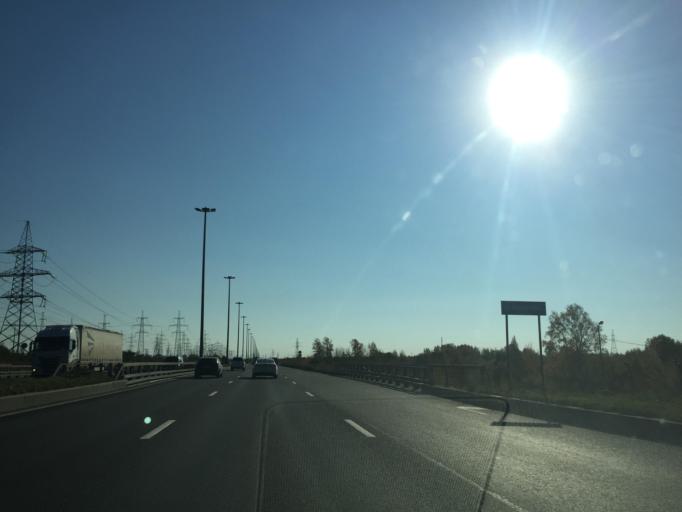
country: RU
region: St.-Petersburg
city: Petro-Slavyanka
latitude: 59.7636
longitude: 30.5066
